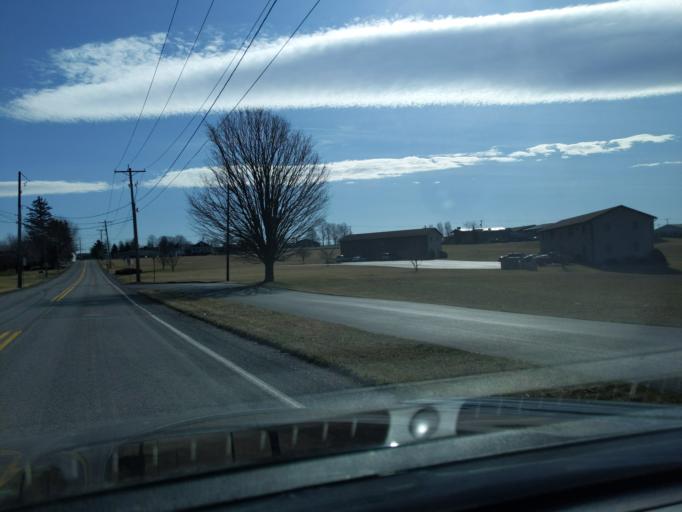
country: US
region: Pennsylvania
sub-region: Blair County
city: Martinsburg
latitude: 40.3022
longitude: -78.3331
